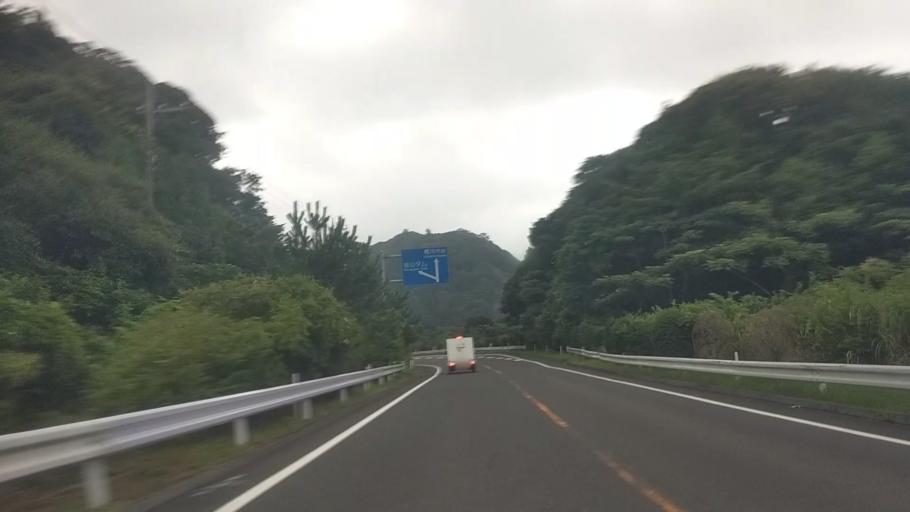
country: JP
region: Chiba
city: Kawaguchi
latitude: 35.1593
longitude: 140.0657
